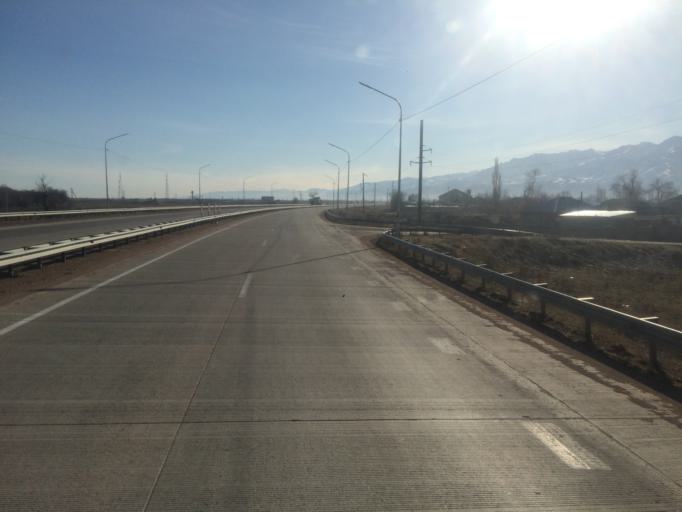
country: KG
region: Talas
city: Ivanovo-Alekseyevka
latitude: 42.9953
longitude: 72.1067
